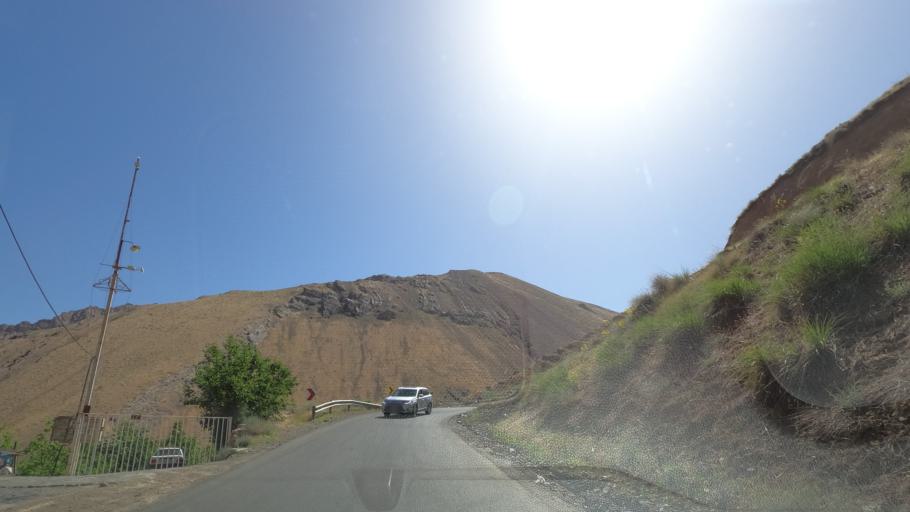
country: IR
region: Alborz
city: Karaj
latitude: 35.9404
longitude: 51.0866
